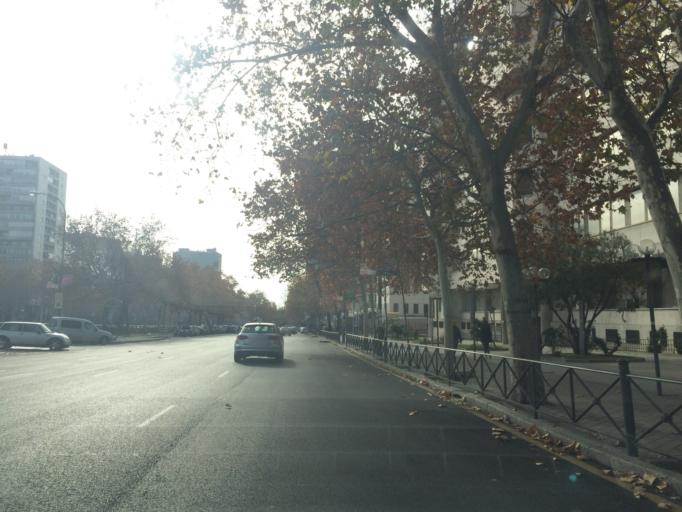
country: ES
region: Madrid
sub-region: Provincia de Madrid
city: Chamartin
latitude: 40.4653
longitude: -3.6898
